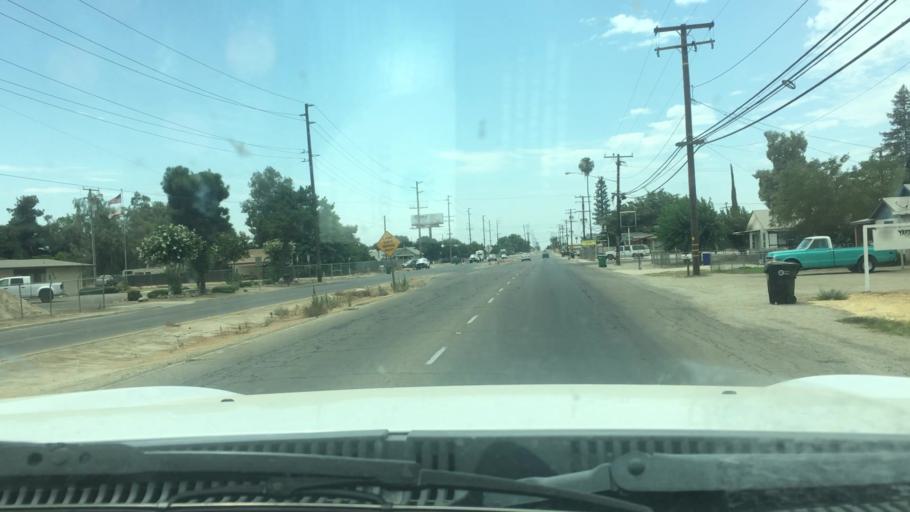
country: US
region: California
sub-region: Tulare County
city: Porterville
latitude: 36.0659
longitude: -119.0720
